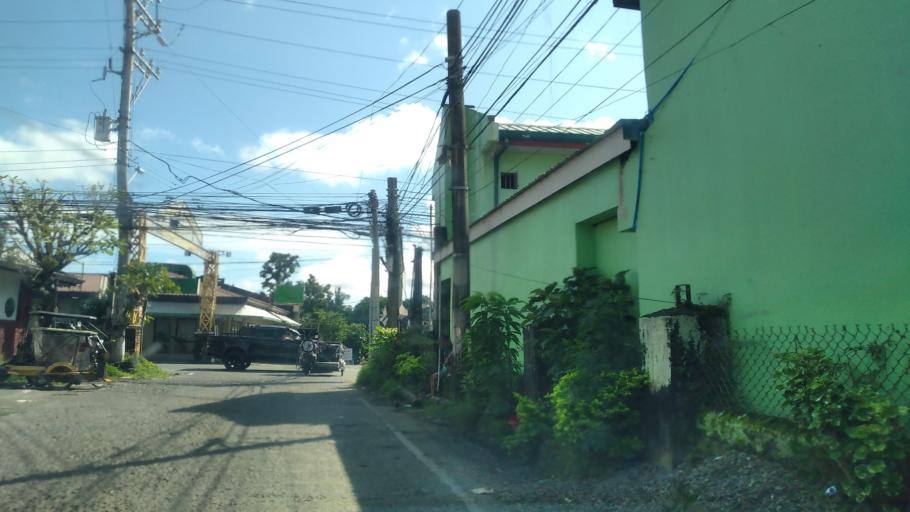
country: PH
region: Calabarzon
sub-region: Province of Quezon
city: Lucena
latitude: 13.9428
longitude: 121.6134
